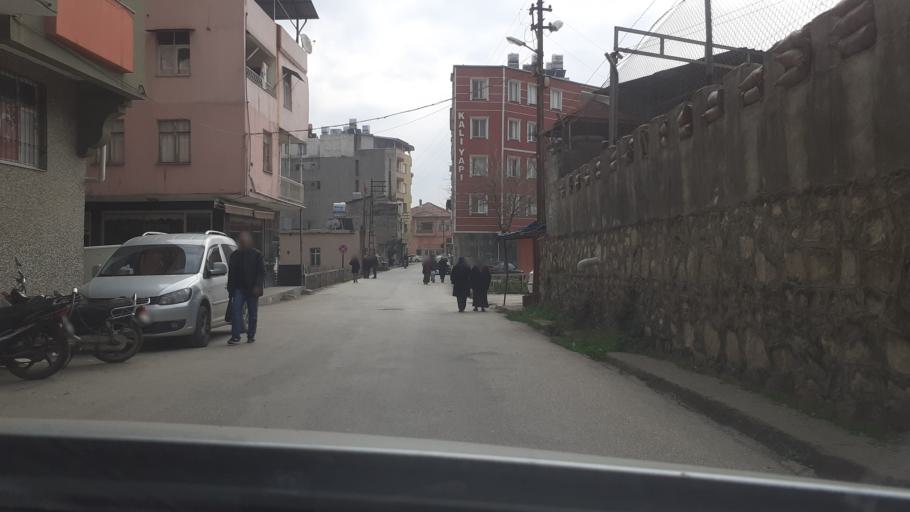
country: TR
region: Hatay
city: Kirikhan
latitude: 36.4976
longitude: 36.3539
